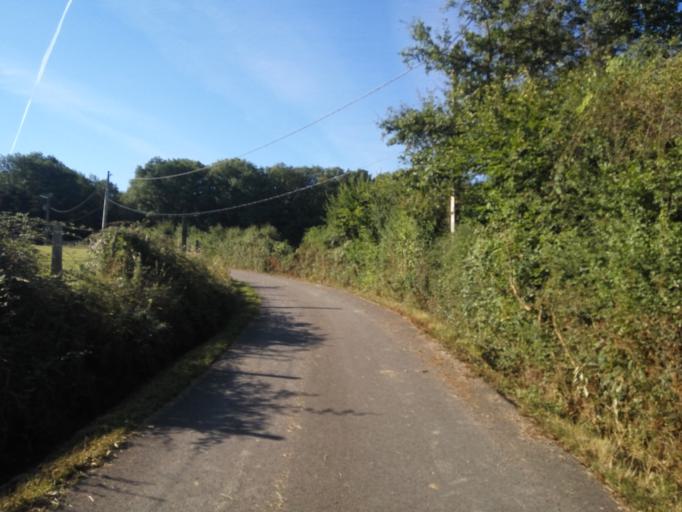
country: FR
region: Auvergne
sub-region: Departement de l'Allier
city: Brugheas
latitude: 46.0925
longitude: 3.3597
